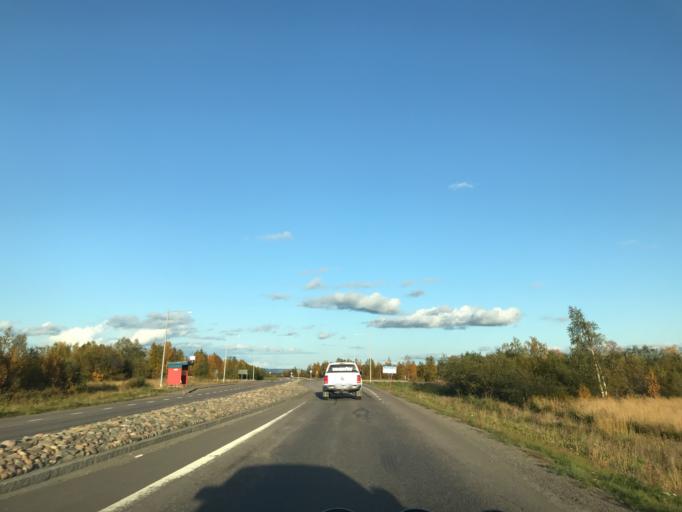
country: SE
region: Norrbotten
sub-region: Kiruna Kommun
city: Kiruna
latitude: 67.8456
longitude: 20.3457
